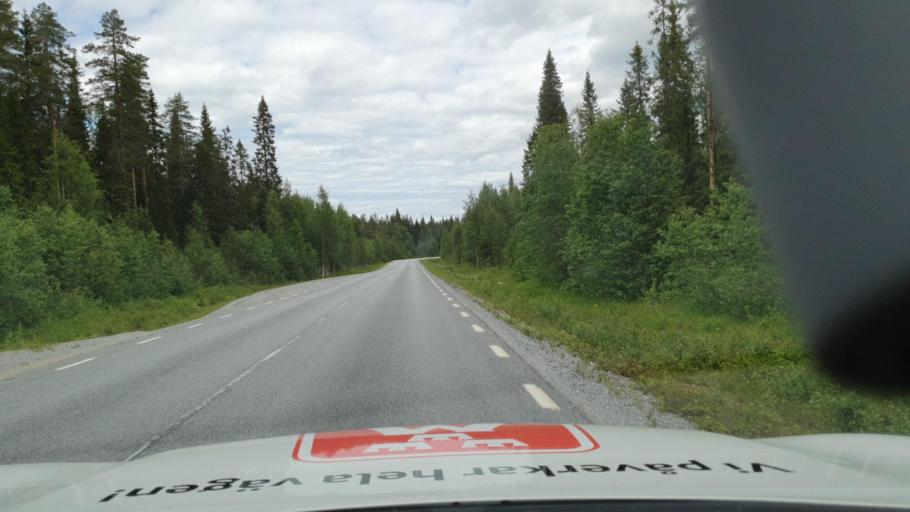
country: SE
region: Vaesterbotten
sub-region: Bjurholms Kommun
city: Bjurholm
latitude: 63.8928
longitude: 19.0642
